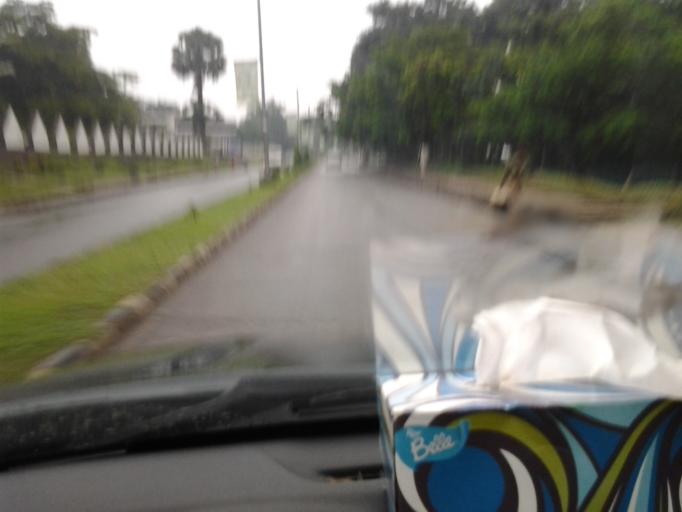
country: NG
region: Oyo
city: Ibadan
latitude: 7.4492
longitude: 3.8998
